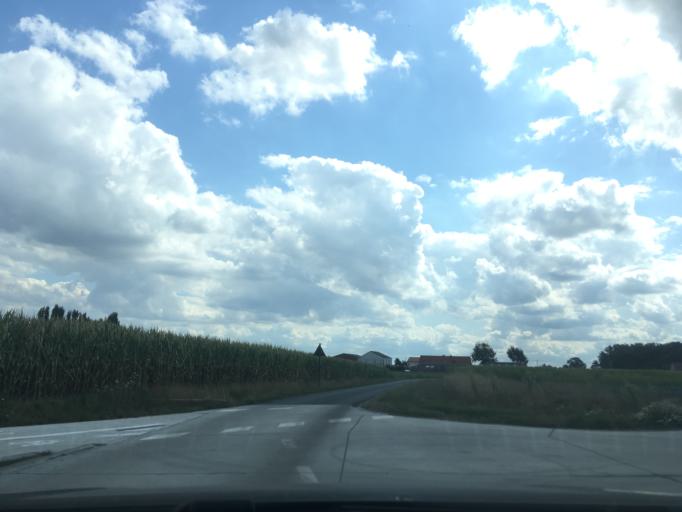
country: BE
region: Flanders
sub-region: Provincie West-Vlaanderen
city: Staden
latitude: 50.9394
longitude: 3.0269
